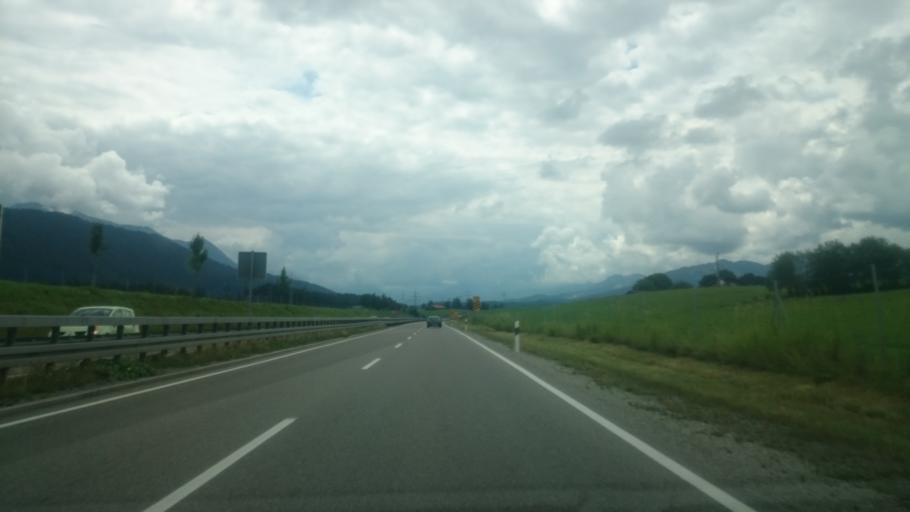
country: DE
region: Bavaria
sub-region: Swabia
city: Rettenberg
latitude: 47.6199
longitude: 10.2760
